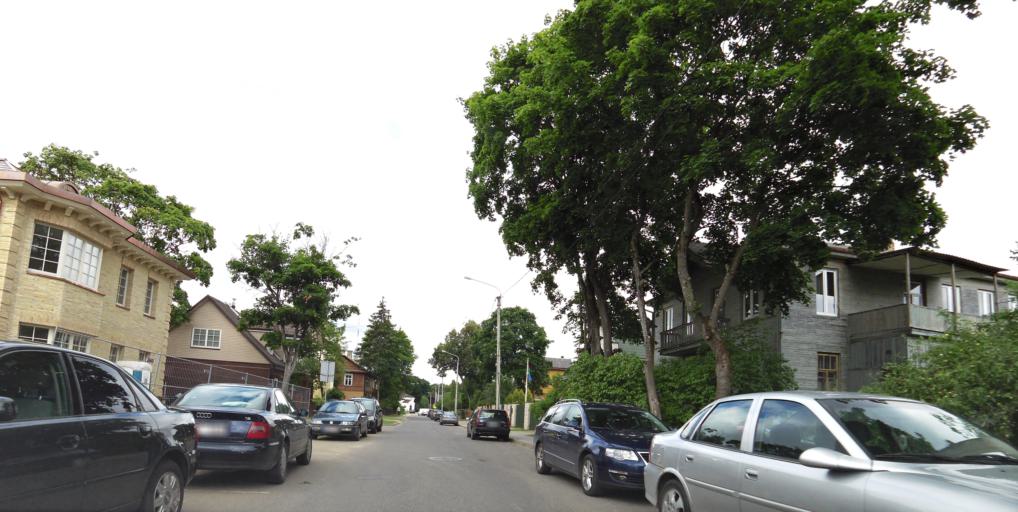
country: LT
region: Vilnius County
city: Seskine
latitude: 54.6930
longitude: 25.2484
